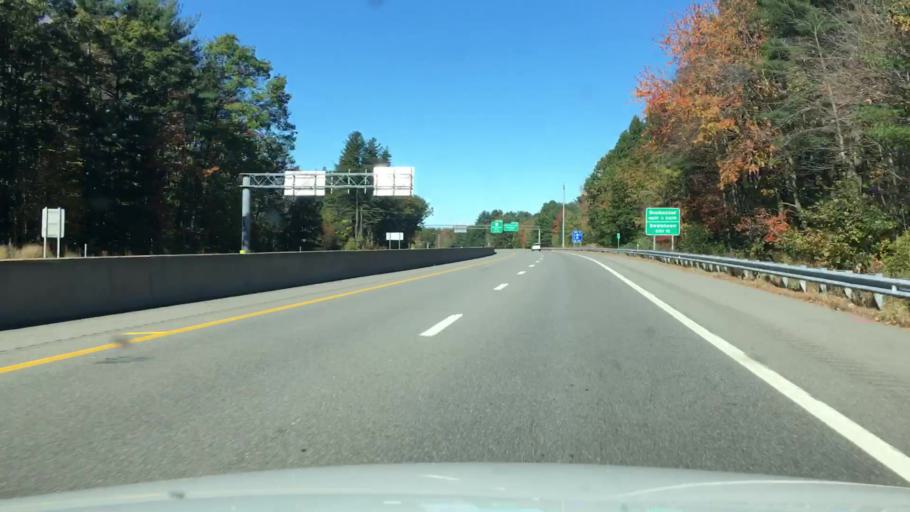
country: US
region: New Hampshire
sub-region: Strafford County
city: Rochester
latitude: 43.2764
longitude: -70.9664
